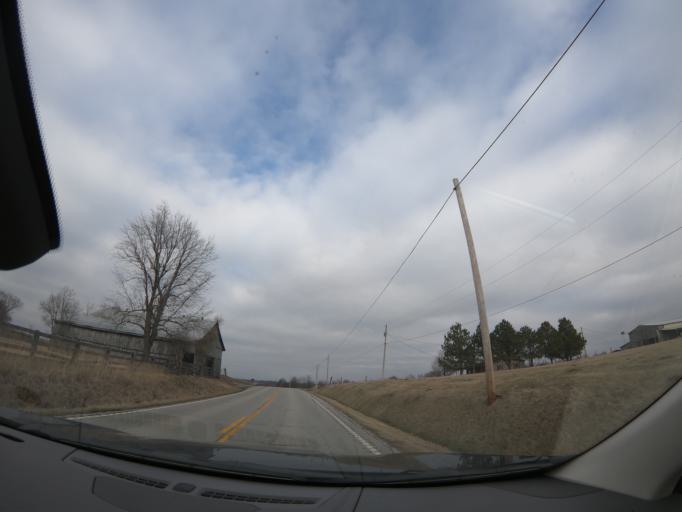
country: US
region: Kentucky
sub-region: Spencer County
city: Taylorsville
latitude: 37.8740
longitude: -85.3111
